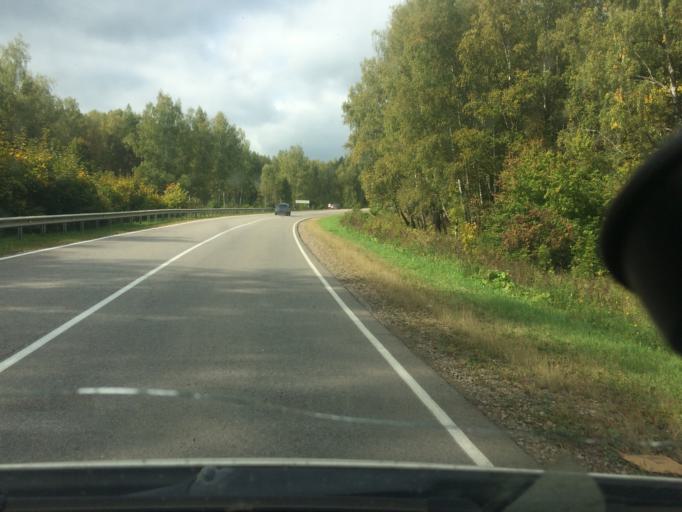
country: RU
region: Tula
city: Suvorov
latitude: 54.0537
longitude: 36.5714
